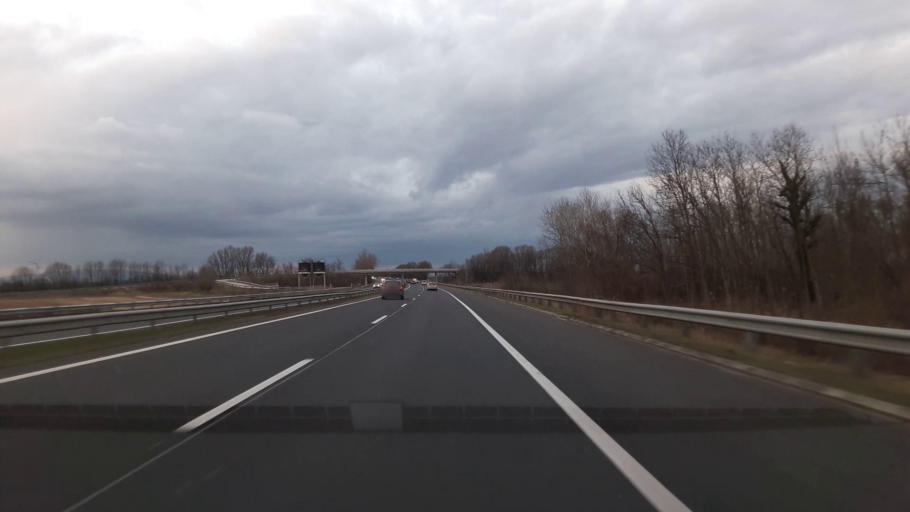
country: AT
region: Burgenland
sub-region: Eisenstadt-Umgebung
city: Wimpassing an der Leitha
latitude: 47.9040
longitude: 16.4127
